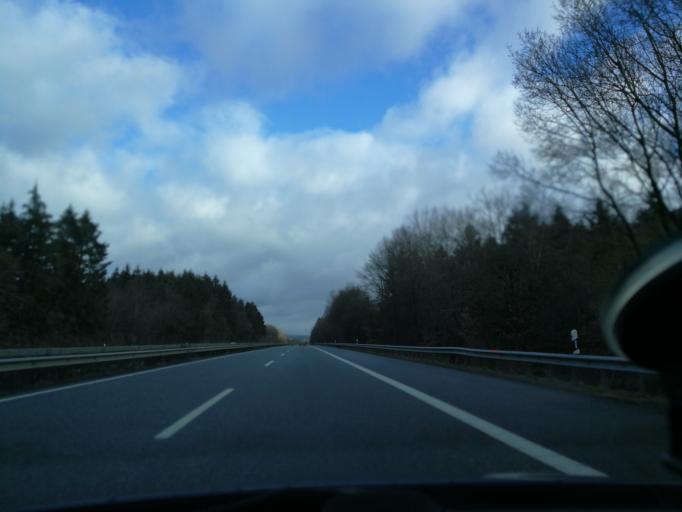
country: DE
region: Rheinland-Pfalz
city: Brockscheid
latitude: 50.1265
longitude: 6.8567
